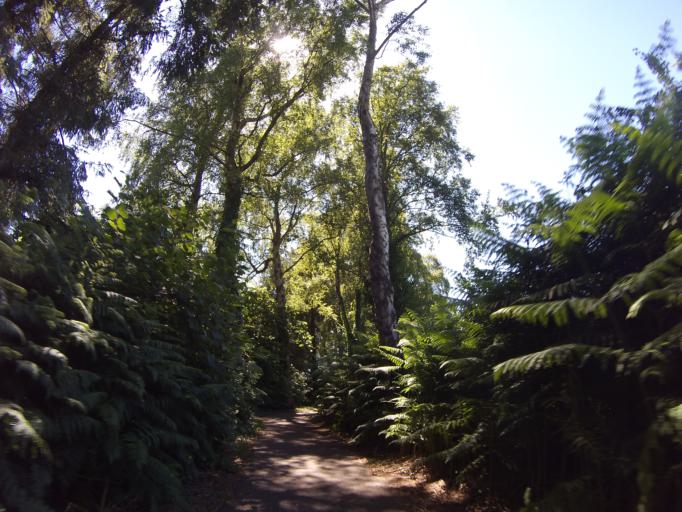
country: NL
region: Drenthe
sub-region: Gemeente Assen
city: Assen
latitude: 52.9762
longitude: 6.5657
